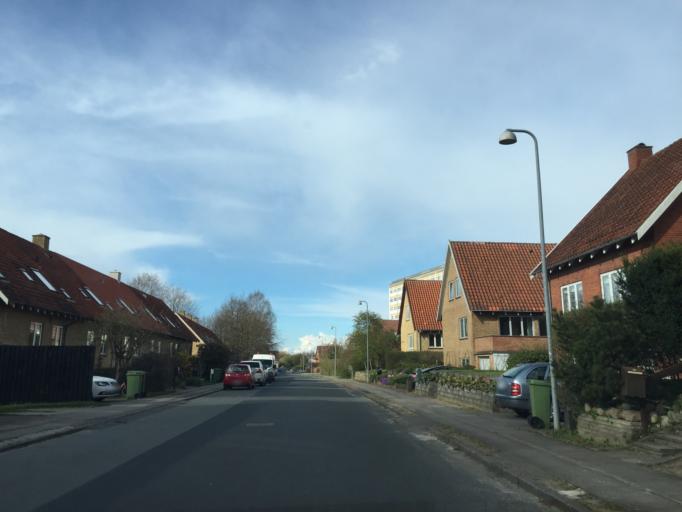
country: DK
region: South Denmark
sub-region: Odense Kommune
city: Odense
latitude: 55.3915
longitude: 10.4159
